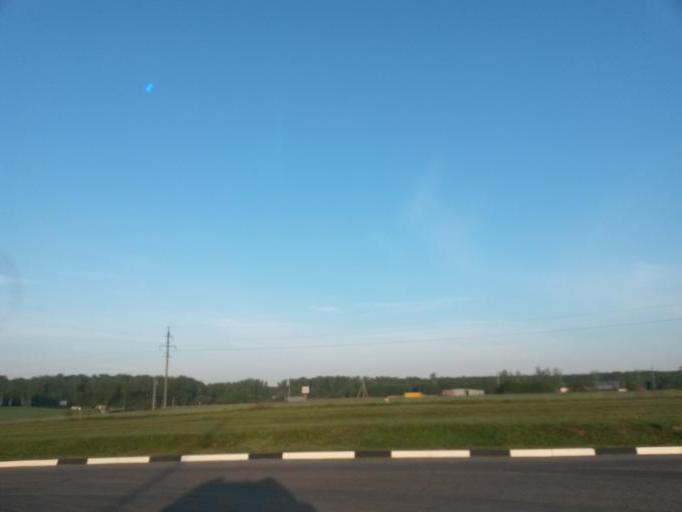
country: RU
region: Moskovskaya
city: Lyubuchany
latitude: 55.2511
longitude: 37.5340
